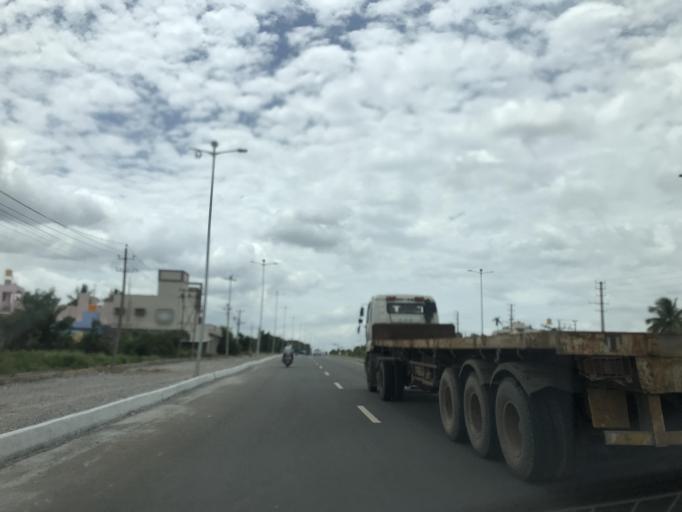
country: IN
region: Karnataka
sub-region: Tumkur
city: Tumkur
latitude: 13.3092
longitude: 77.1397
